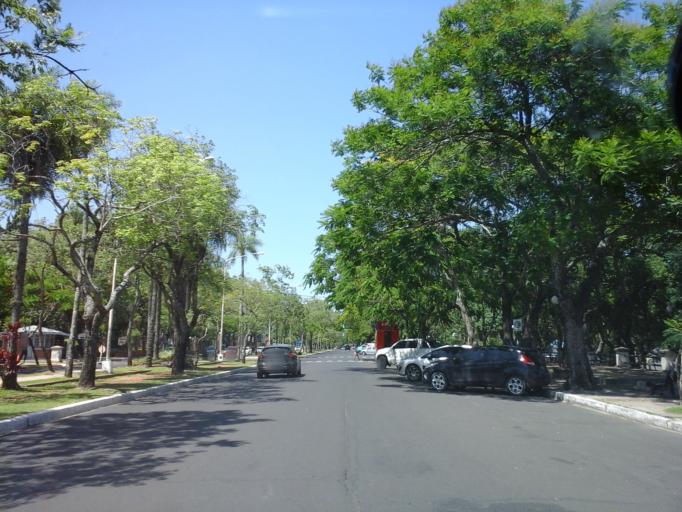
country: AR
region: Corrientes
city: Corrientes
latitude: -27.4681
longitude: -58.8525
